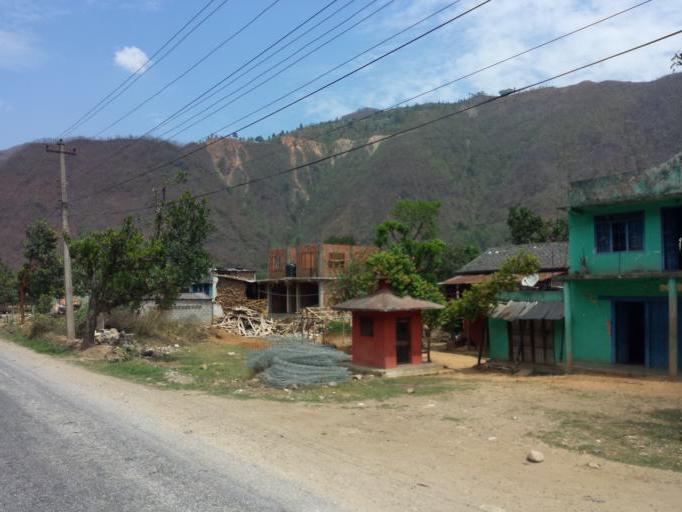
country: NP
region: Central Region
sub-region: Narayani Zone
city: Bharatpur
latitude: 27.8127
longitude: 84.7648
